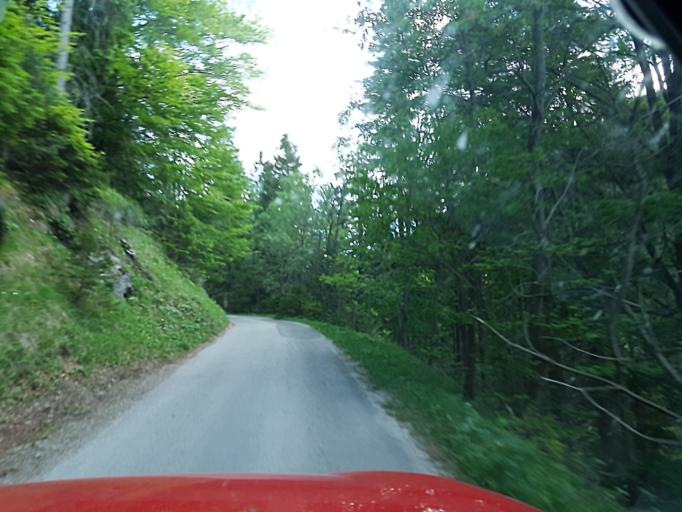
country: SK
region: Zilinsky
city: Ruzomberok
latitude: 49.0567
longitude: 19.2758
